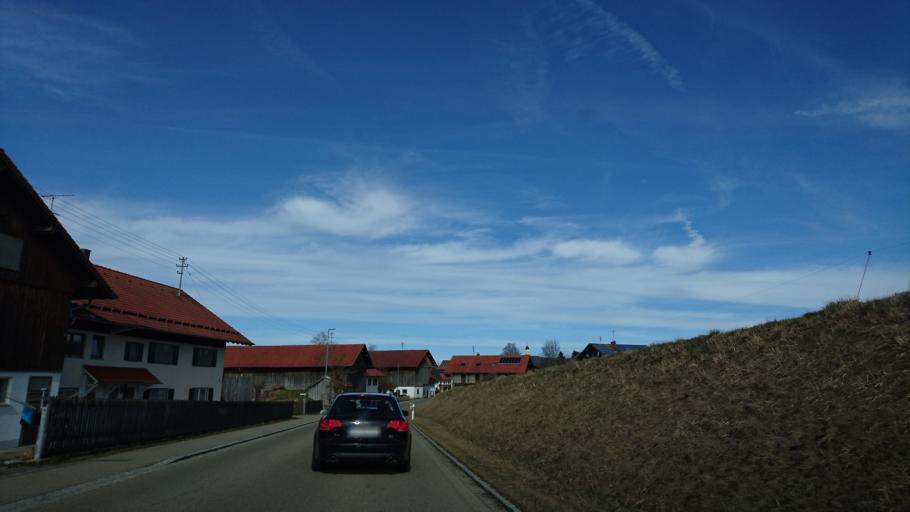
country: DE
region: Bavaria
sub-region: Swabia
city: Lechbruck
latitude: 47.7104
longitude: 10.7776
